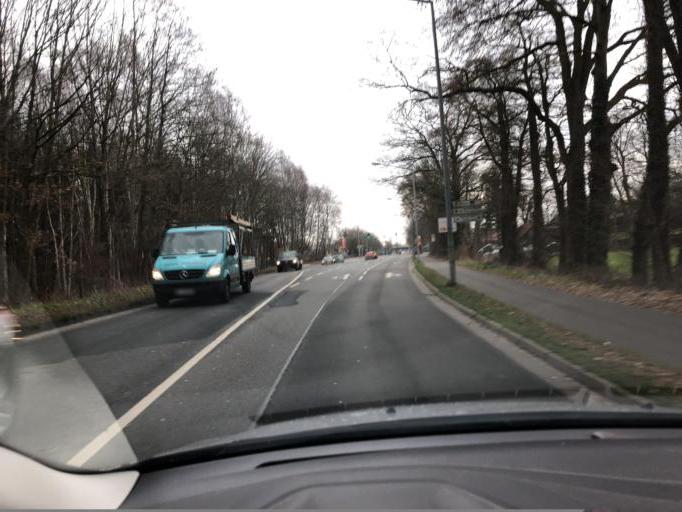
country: DE
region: Lower Saxony
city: Oldenburg
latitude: 53.1622
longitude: 8.1660
